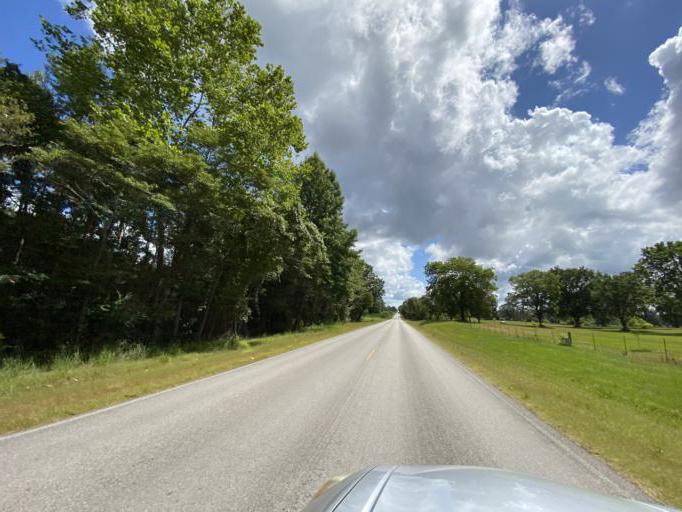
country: US
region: Mississippi
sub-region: Panola County
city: Como
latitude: 34.5104
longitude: -89.9996
